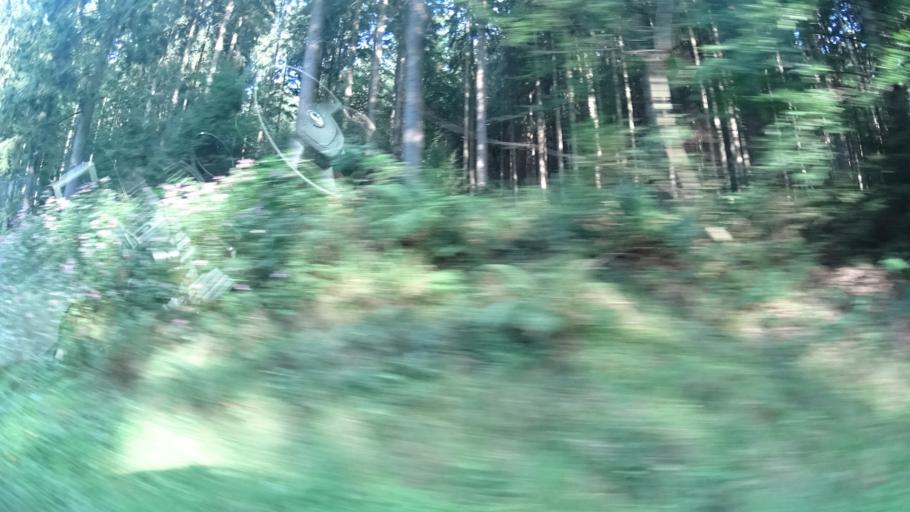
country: DE
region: Baden-Wuerttemberg
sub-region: Karlsruhe Region
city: Heddesbach
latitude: 49.5001
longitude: 8.8484
